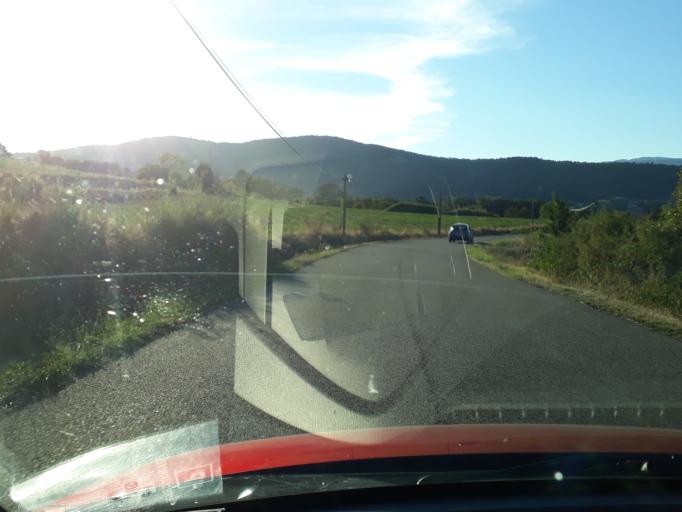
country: FR
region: Rhone-Alpes
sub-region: Departement de l'Ardeche
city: Felines
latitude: 45.3189
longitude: 4.7194
